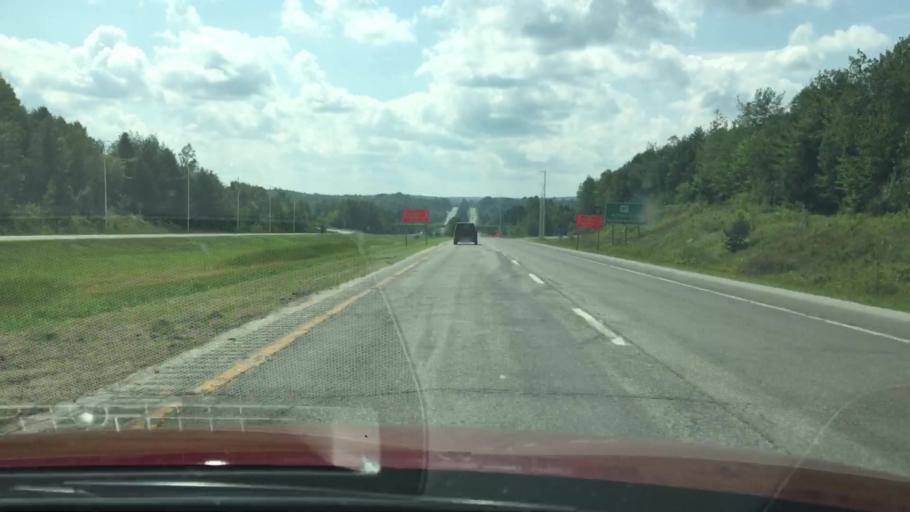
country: US
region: Maine
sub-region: Penobscot County
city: Medway
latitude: 45.6112
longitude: -68.5170
